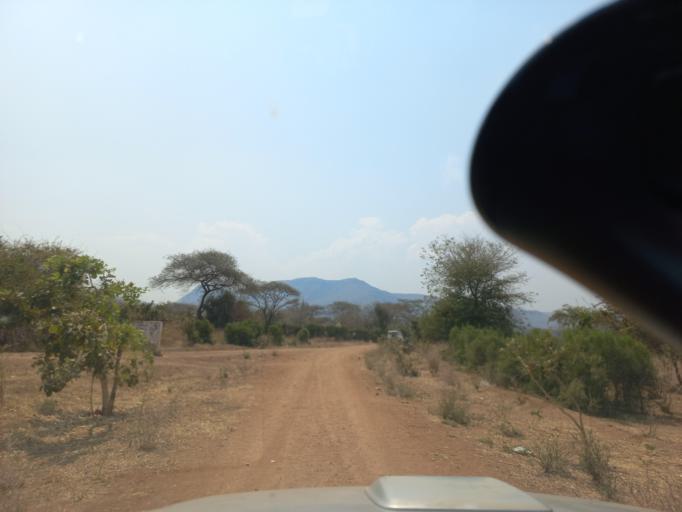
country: ZW
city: Chirundu
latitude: -15.9085
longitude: 28.6861
